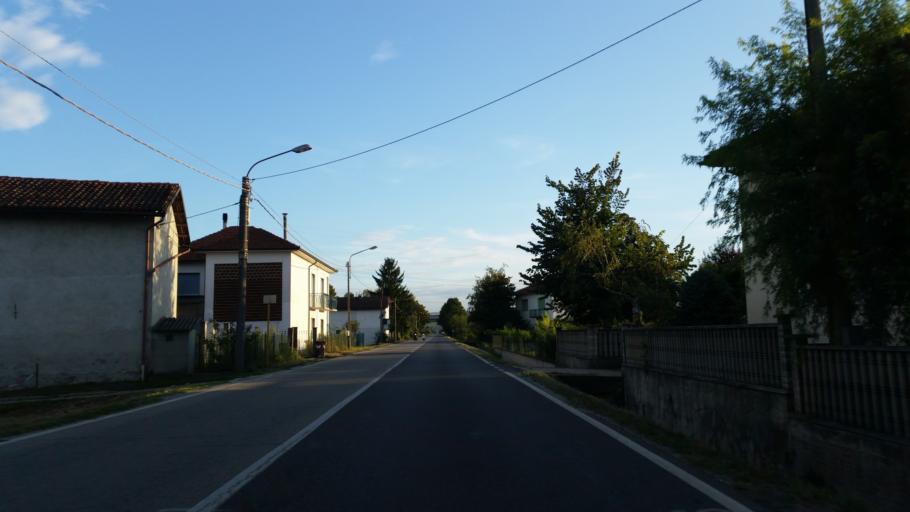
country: IT
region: Piedmont
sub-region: Provincia di Asti
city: Mongardino
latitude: 44.8583
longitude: 8.2023
